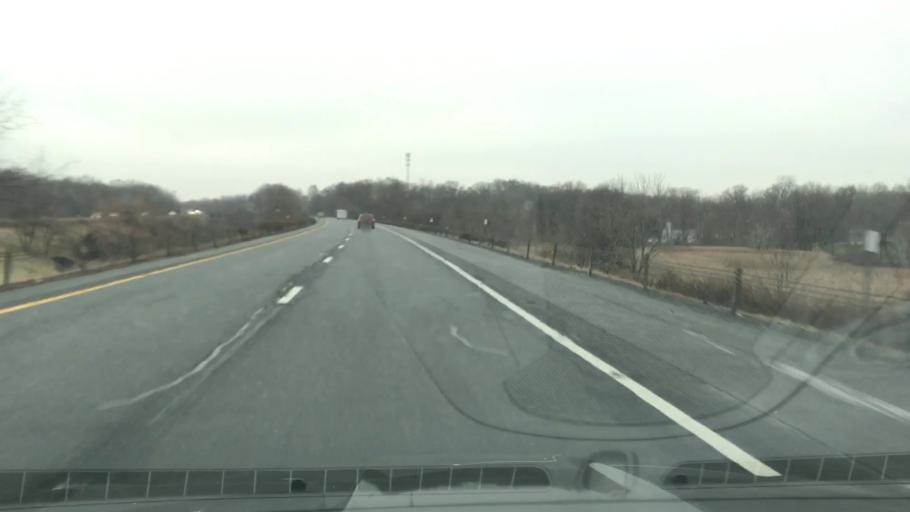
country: US
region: New York
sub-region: Orange County
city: Middletown
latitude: 41.4071
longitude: -74.4876
